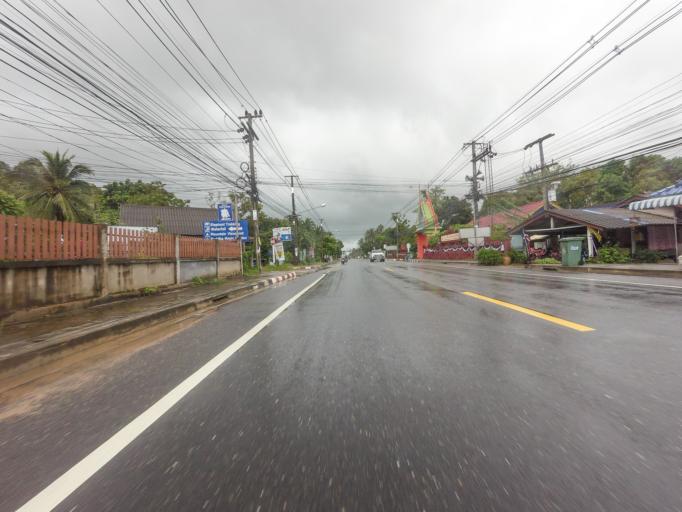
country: TH
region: Surat Thani
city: Ko Samui
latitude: 9.4505
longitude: 100.0010
